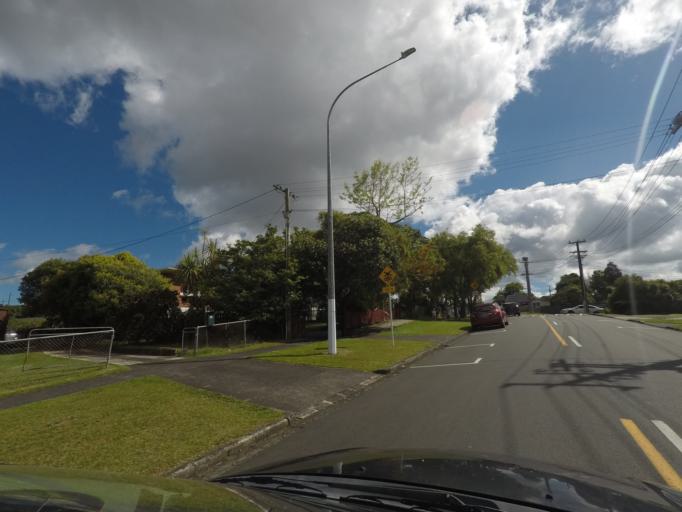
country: NZ
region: Auckland
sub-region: Auckland
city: Waitakere
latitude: -36.9117
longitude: 174.6678
